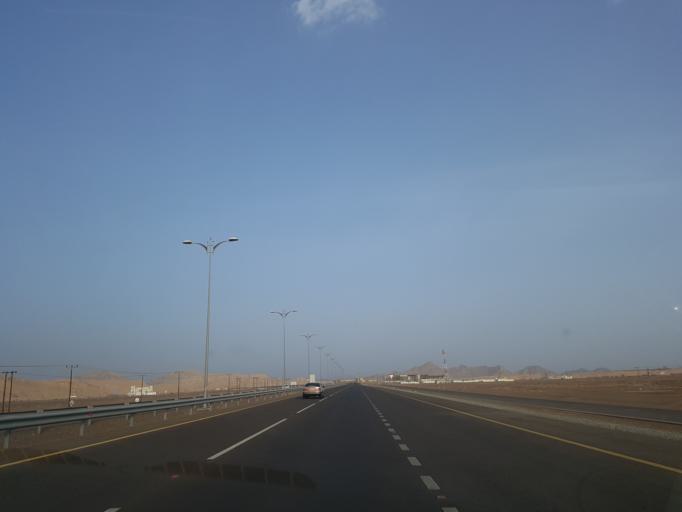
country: OM
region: Al Buraimi
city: Al Buraymi
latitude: 24.2340
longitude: 55.9202
